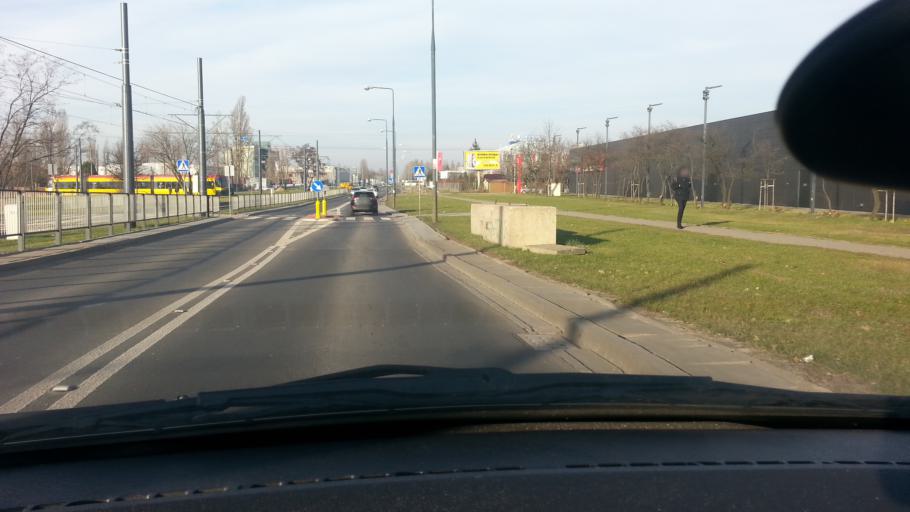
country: PL
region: Masovian Voivodeship
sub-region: Warszawa
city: Targowek
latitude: 52.2985
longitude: 21.0236
